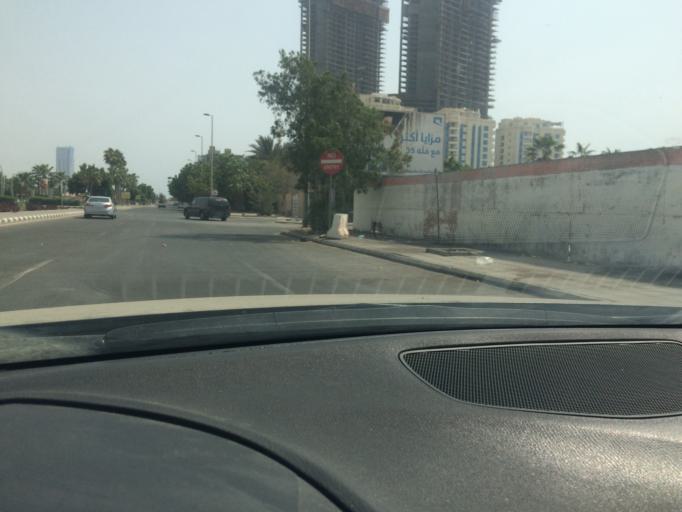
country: SA
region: Makkah
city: Jeddah
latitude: 21.5981
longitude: 39.1092
